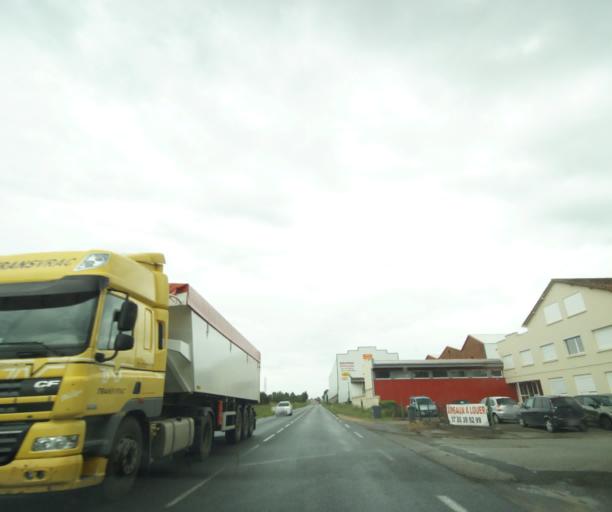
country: FR
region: Poitou-Charentes
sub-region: Departement des Deux-Sevres
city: Chatillon-sur-Thouet
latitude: 46.6686
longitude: -0.2465
